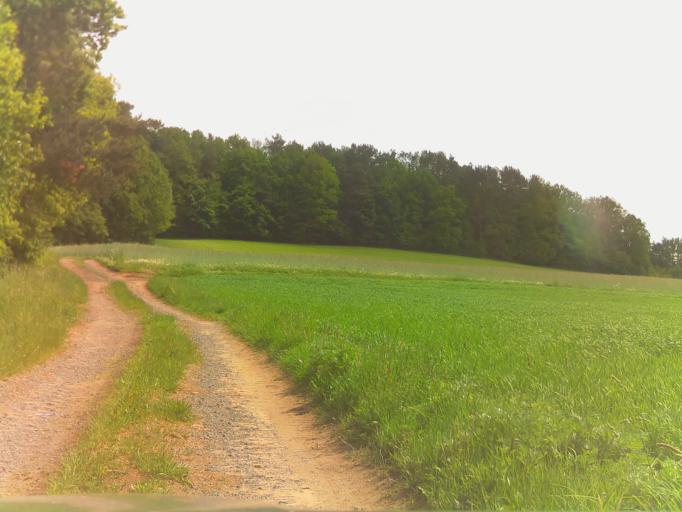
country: DE
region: Bavaria
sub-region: Regierungsbezirk Unterfranken
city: Aura im Sinngrund
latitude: 50.2172
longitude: 9.4961
